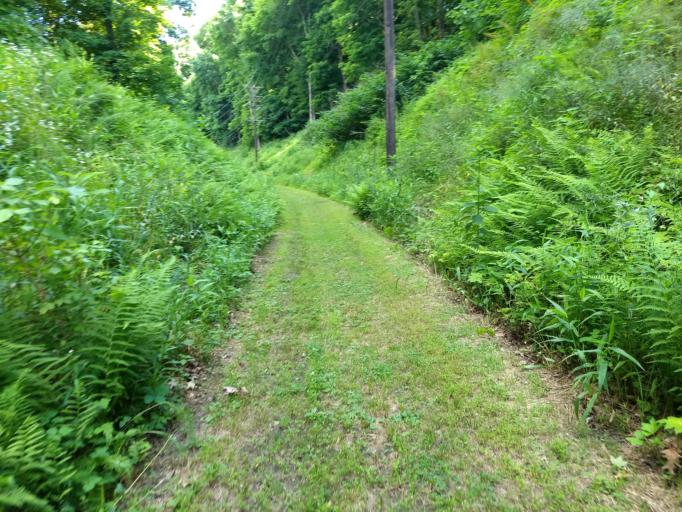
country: US
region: Pennsylvania
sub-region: Westmoreland County
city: Irwin
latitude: 40.3344
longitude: -79.7198
